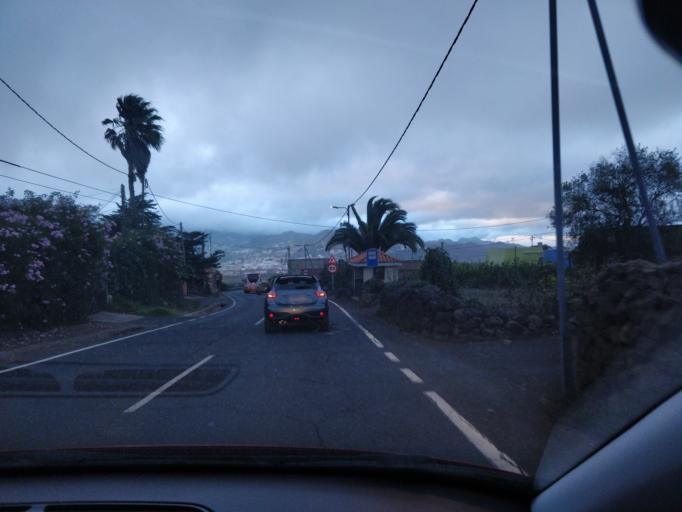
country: ES
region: Canary Islands
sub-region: Provincia de Santa Cruz de Tenerife
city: La Laguna
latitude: 28.4761
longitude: -16.3330
